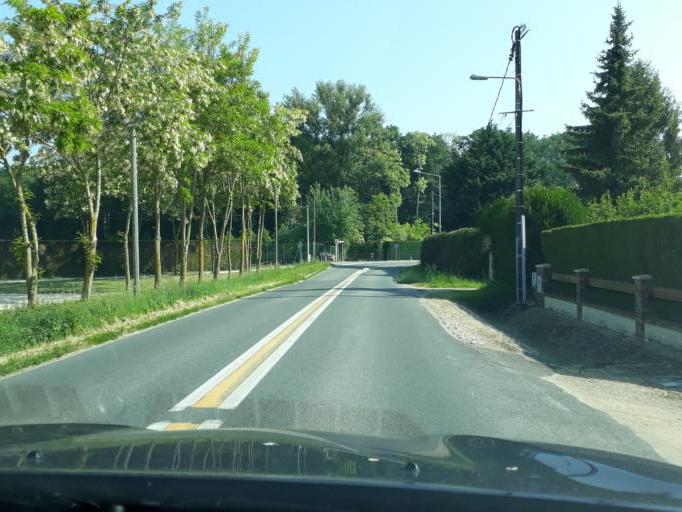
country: FR
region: Centre
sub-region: Departement du Loiret
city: Boigny-sur-Bionne
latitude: 47.9265
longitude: 2.0253
